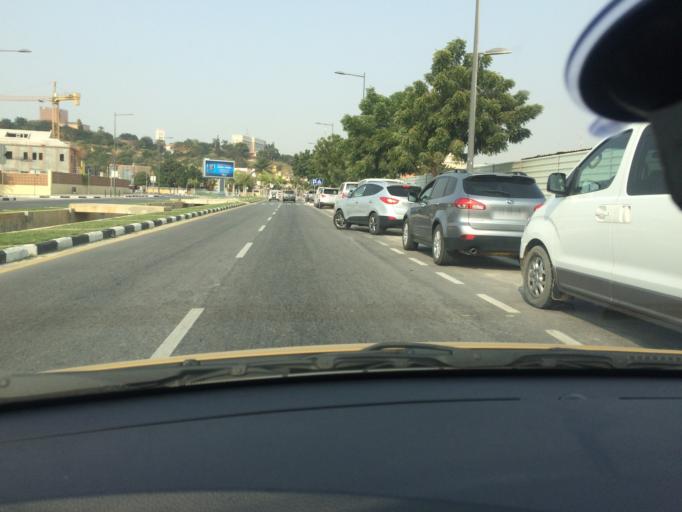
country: AO
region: Luanda
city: Luanda
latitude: -8.8201
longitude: 13.2176
